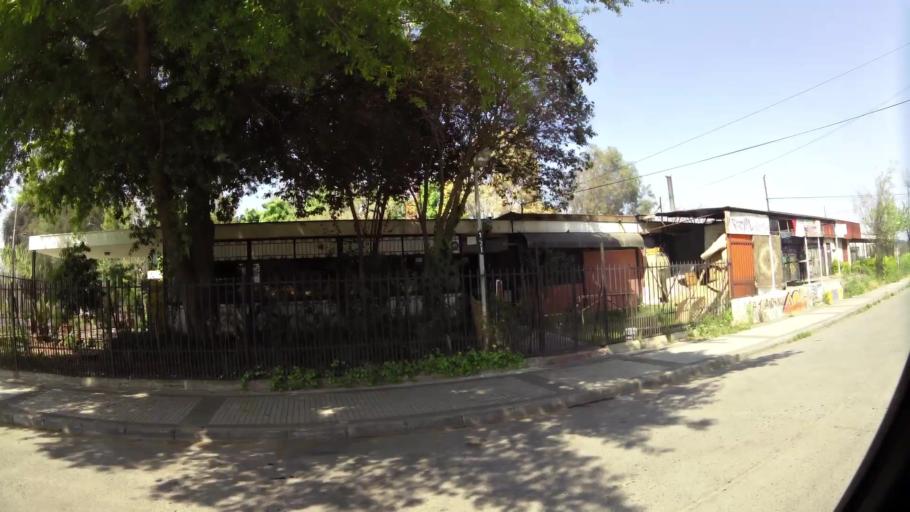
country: CL
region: Santiago Metropolitan
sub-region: Provincia de Santiago
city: Lo Prado
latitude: -33.4449
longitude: -70.6880
